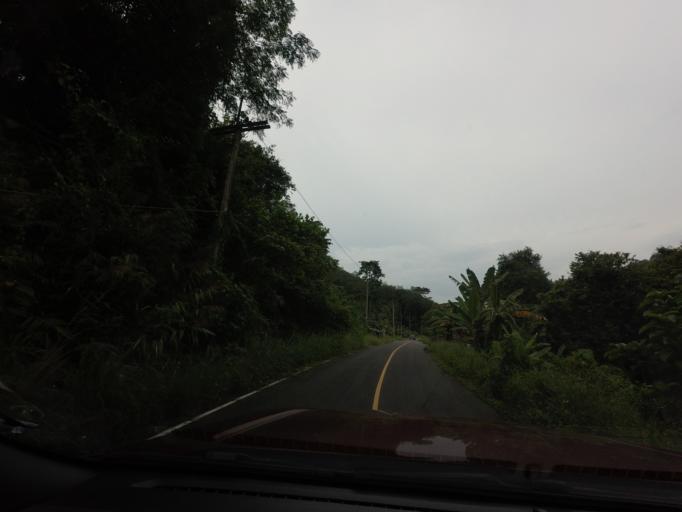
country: TH
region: Narathiwat
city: Si Sakhon
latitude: 6.0623
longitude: 101.3877
